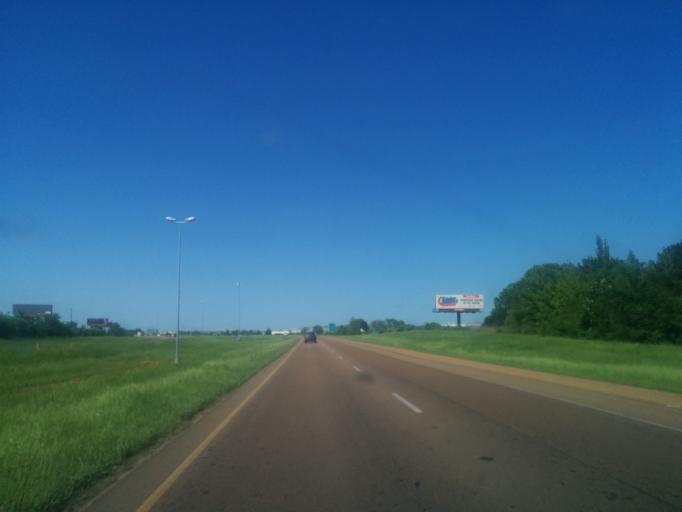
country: US
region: Mississippi
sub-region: Madison County
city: Madison
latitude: 32.5230
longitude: -90.0975
